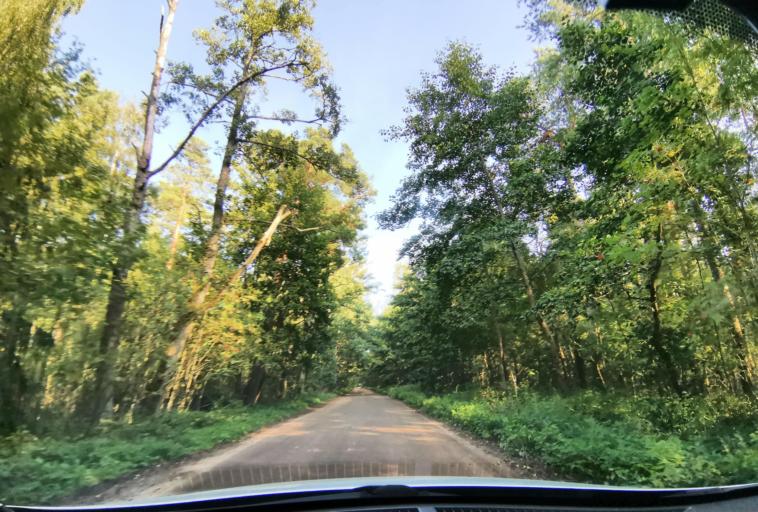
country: LT
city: Nida
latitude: 55.1594
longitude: 20.8372
